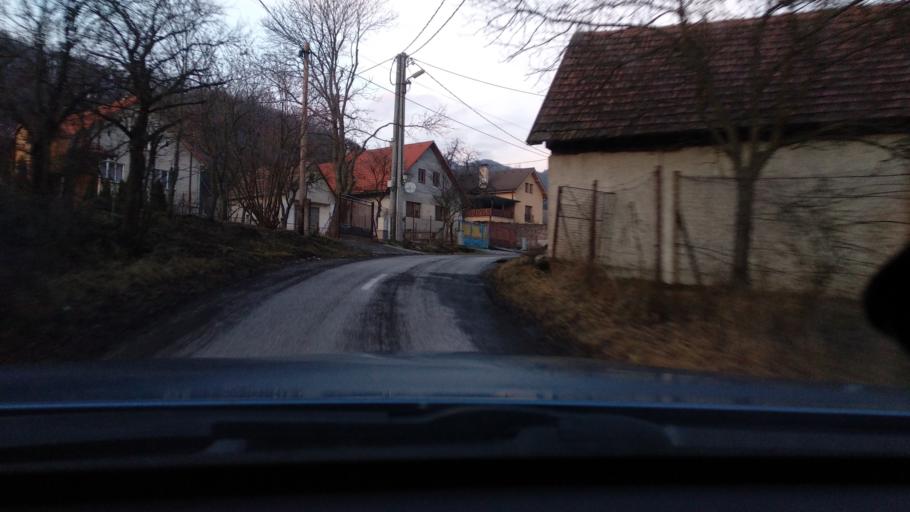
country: SK
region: Nitriansky
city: Ilava
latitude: 48.8694
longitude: 18.3351
